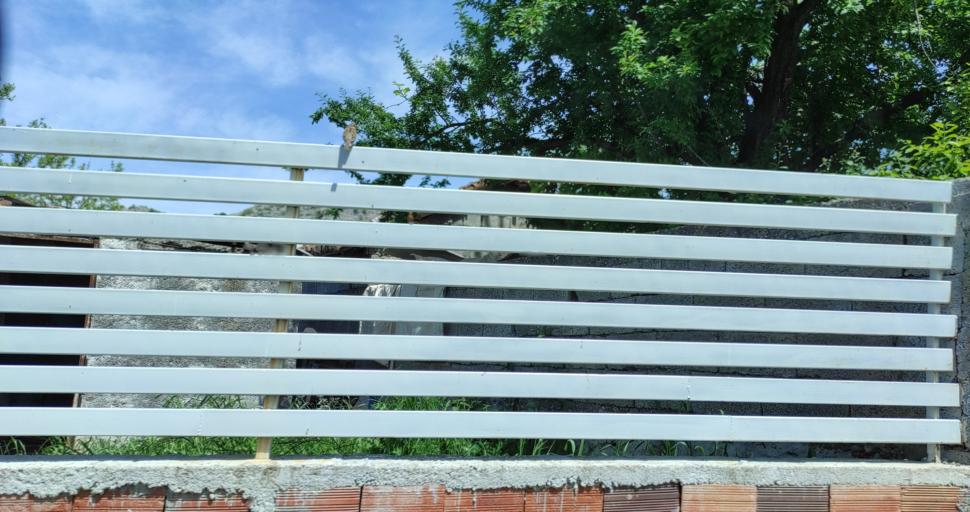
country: AL
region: Shkoder
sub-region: Rrethi i Malesia e Madhe
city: Gruemire
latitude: 42.1475
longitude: 19.5414
